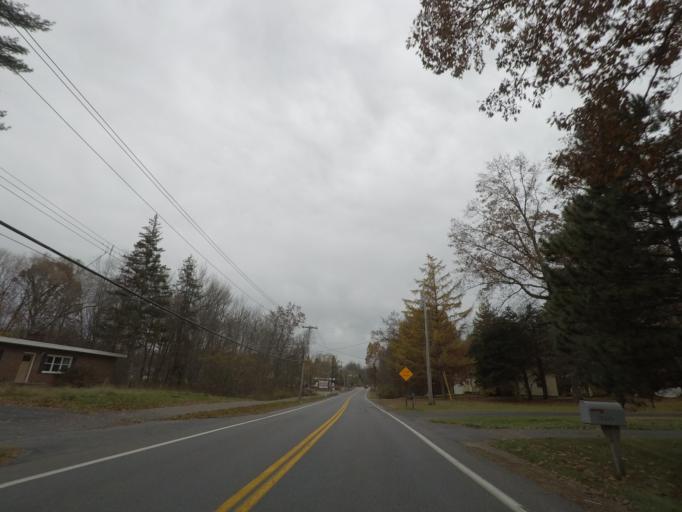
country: US
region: New York
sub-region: Schenectady County
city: Niskayuna
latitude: 42.8388
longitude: -73.8215
